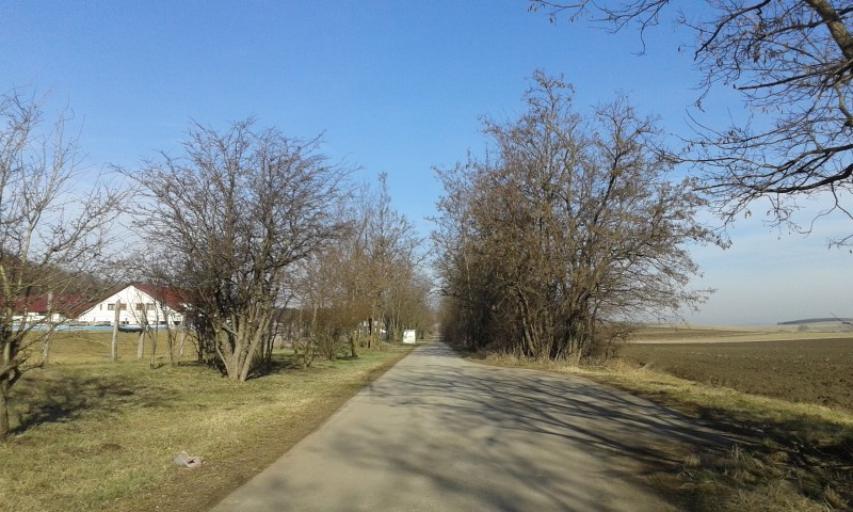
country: HU
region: Fejer
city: Etyek
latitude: 47.4083
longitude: 18.7726
